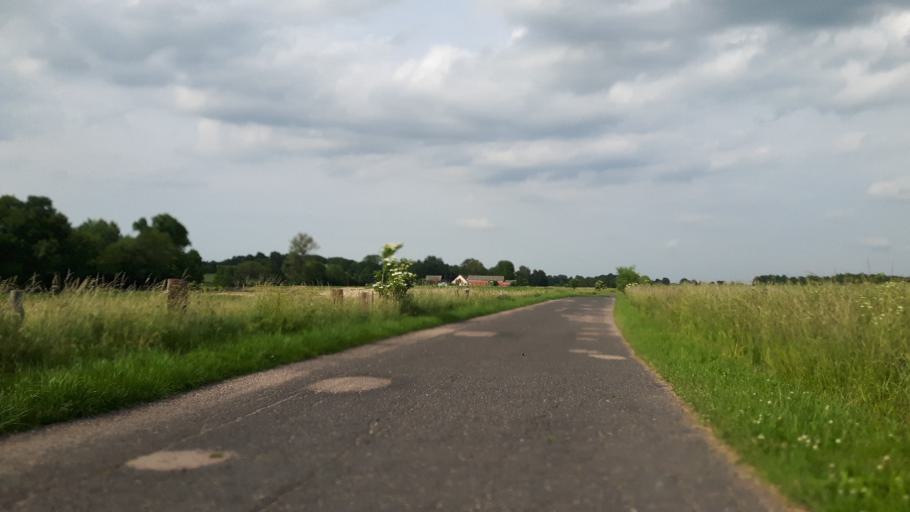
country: PL
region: West Pomeranian Voivodeship
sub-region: Powiat gryficki
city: Gryfice
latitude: 53.8260
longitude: 15.1407
